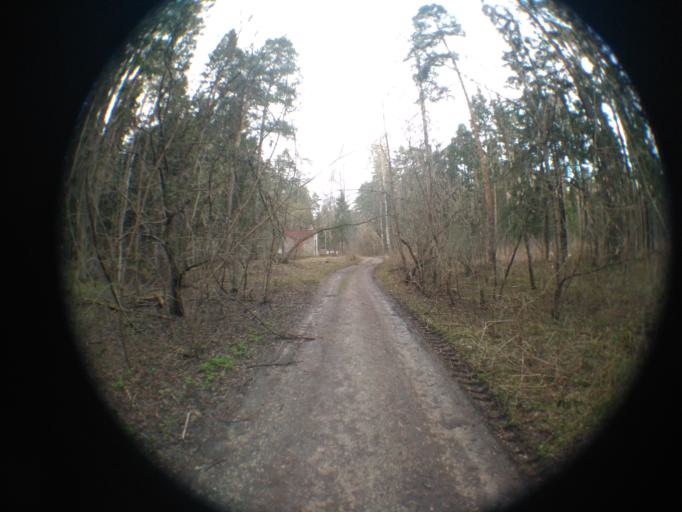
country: RU
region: Moskovskaya
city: Zhukovskiy
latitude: 55.5832
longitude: 38.1128
